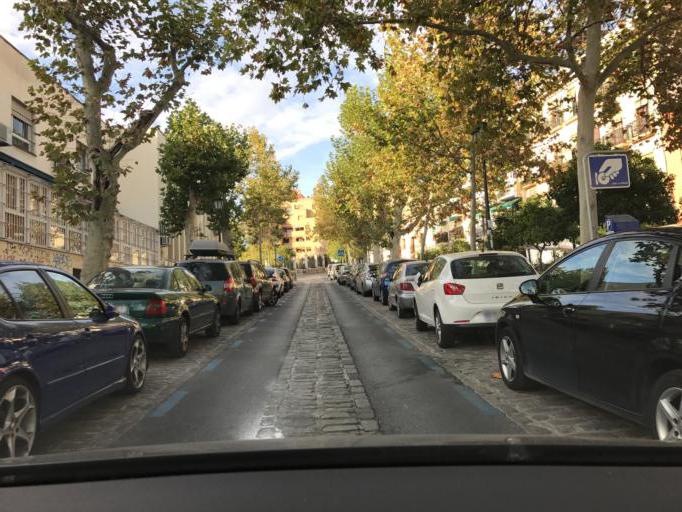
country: ES
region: Andalusia
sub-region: Provincia de Granada
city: Granada
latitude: 37.1840
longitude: -3.6000
